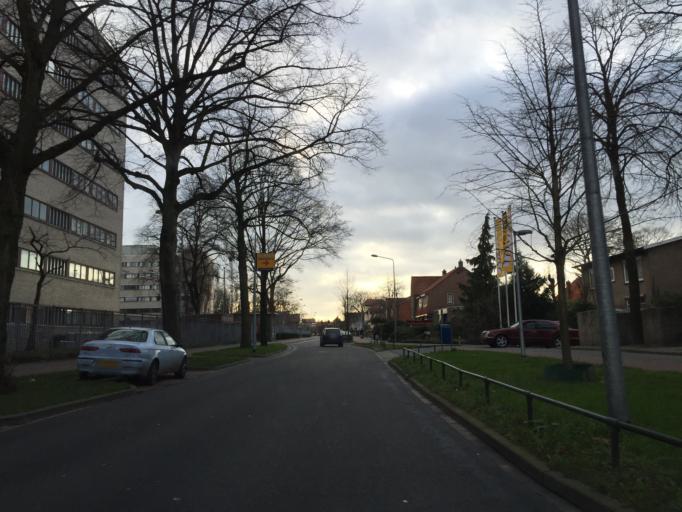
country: NL
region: North Holland
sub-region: Gemeente Hilversum
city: Hilversum
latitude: 52.2327
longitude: 5.1898
